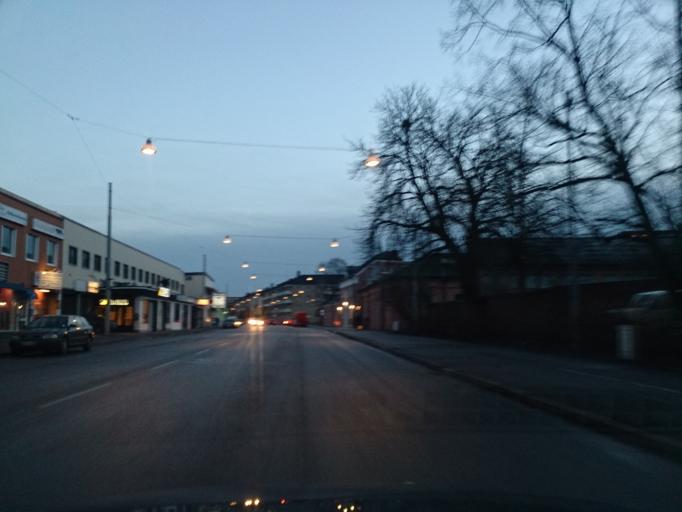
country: SE
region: OEstergoetland
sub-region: Norrkopings Kommun
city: Norrkoping
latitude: 58.5979
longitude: 16.1701
